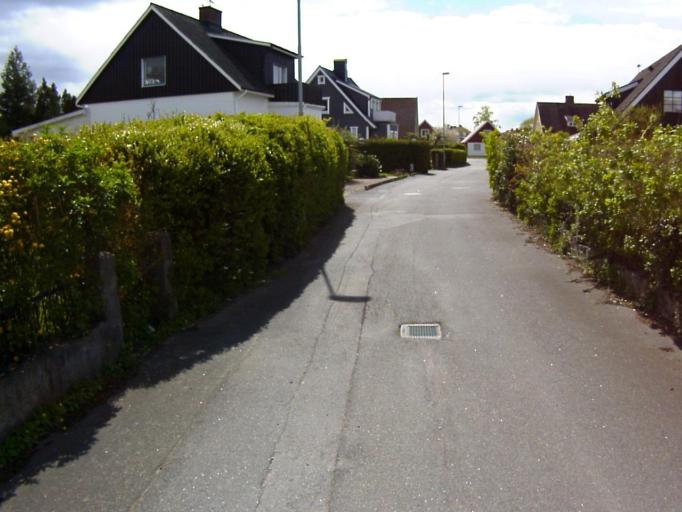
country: SE
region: Skane
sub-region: Kristianstads Kommun
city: Kristianstad
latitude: 56.0374
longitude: 14.1702
